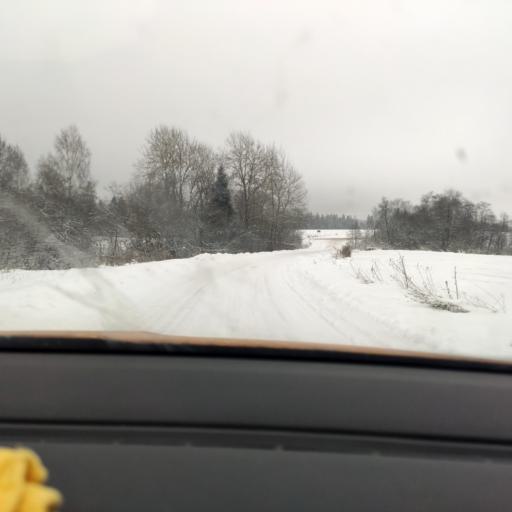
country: RU
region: Moskovskaya
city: Yershovo
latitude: 55.7879
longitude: 36.7842
